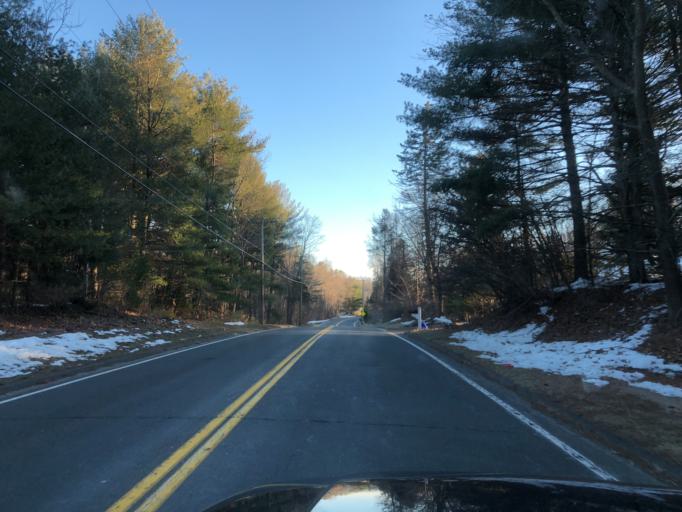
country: US
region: Connecticut
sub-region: Hartford County
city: Farmington
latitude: 41.7591
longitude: -72.8577
